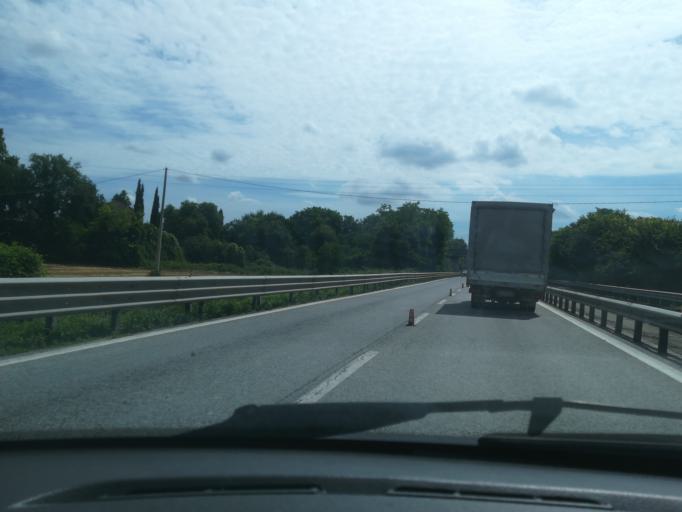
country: IT
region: The Marches
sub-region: Provincia di Macerata
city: Corridonia
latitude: 43.2691
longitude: 13.5102
